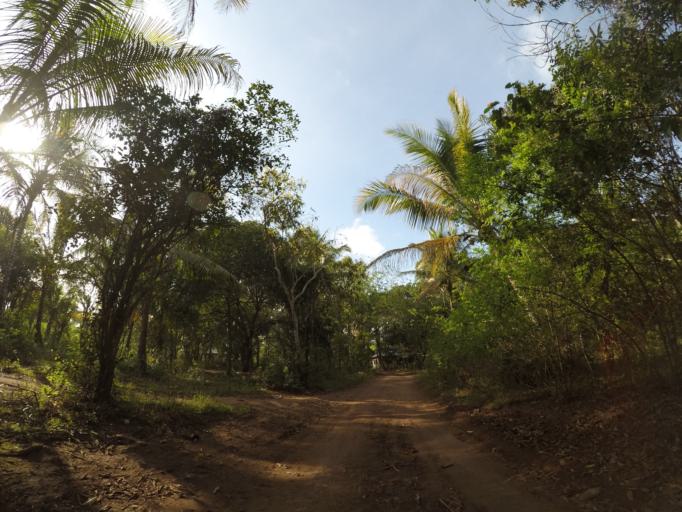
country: TZ
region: Zanzibar Central/South
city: Koani
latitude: -6.2115
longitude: 39.3198
